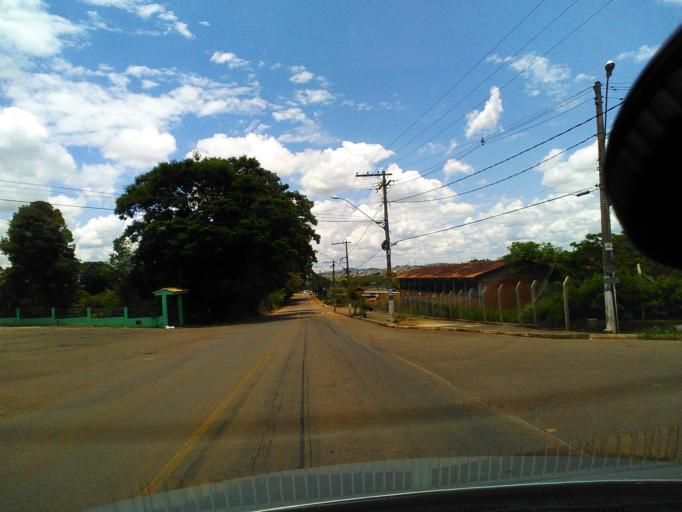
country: BR
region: Minas Gerais
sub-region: Tres Coracoes
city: Tres Coracoes
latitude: -21.7273
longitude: -45.2632
